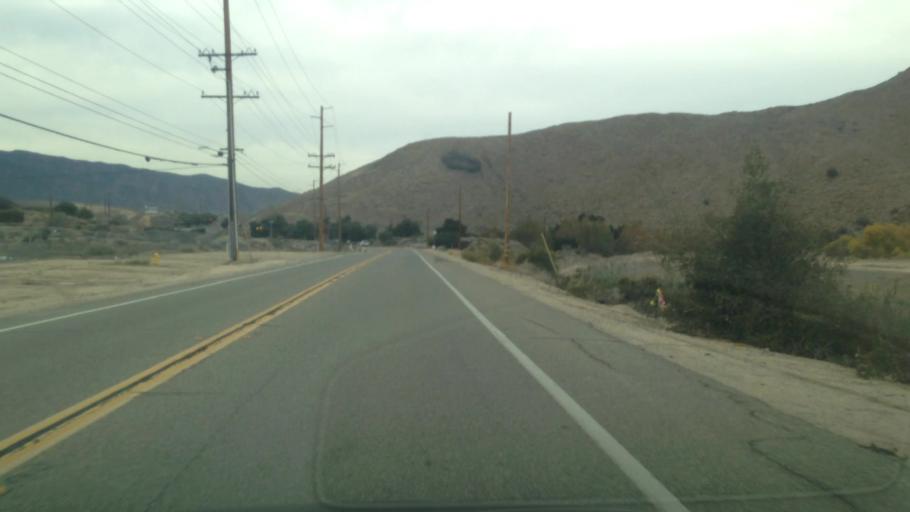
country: US
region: California
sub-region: Riverside County
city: El Cerrito
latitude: 33.7474
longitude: -117.4454
